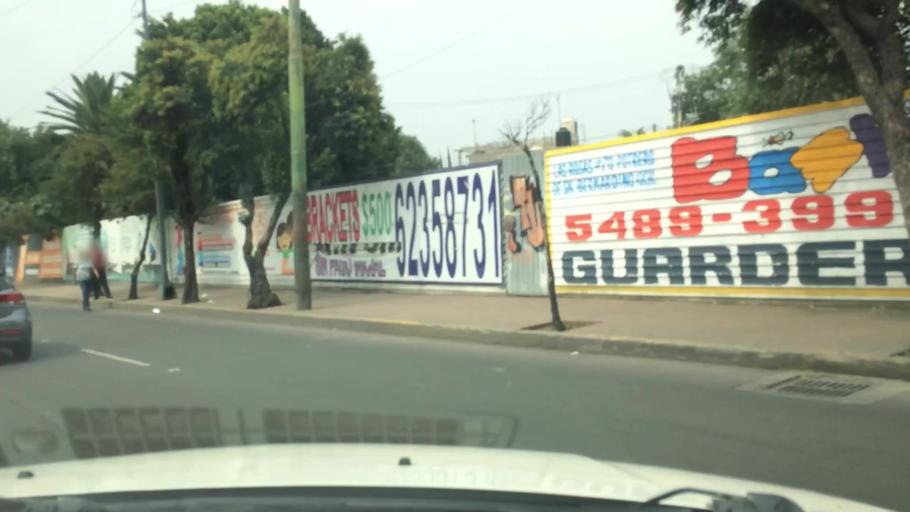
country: MX
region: Mexico City
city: Xochimilco
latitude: 19.2741
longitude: -99.1200
